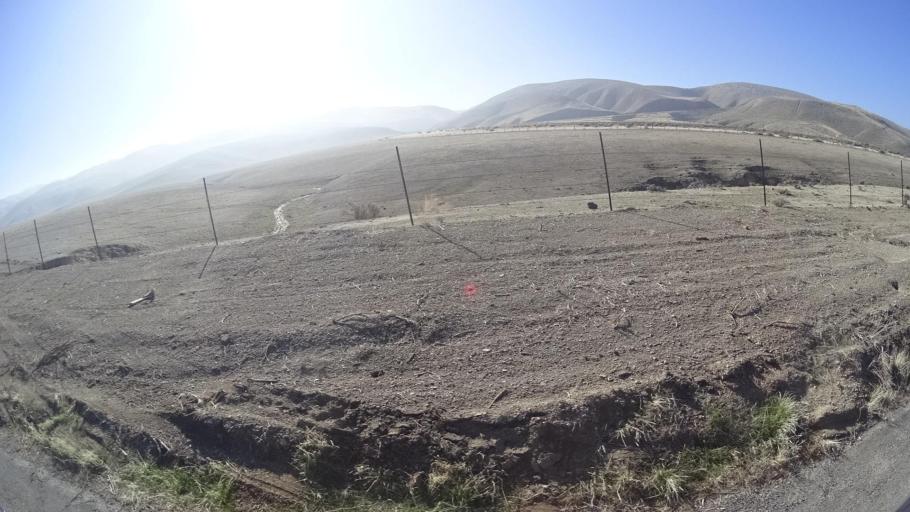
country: US
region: California
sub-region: Kern County
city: Maricopa
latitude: 35.0036
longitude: -119.4067
